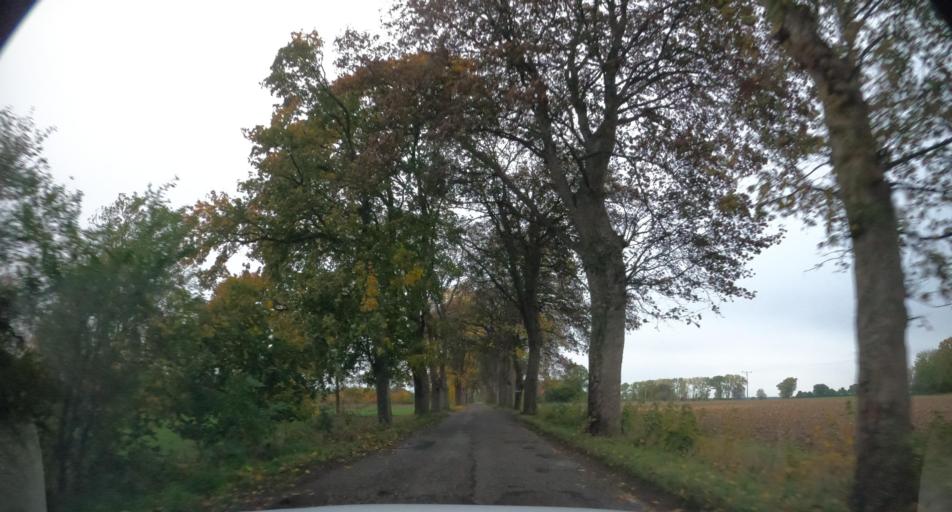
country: PL
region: West Pomeranian Voivodeship
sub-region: Powiat kamienski
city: Wolin
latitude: 53.9065
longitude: 14.6204
